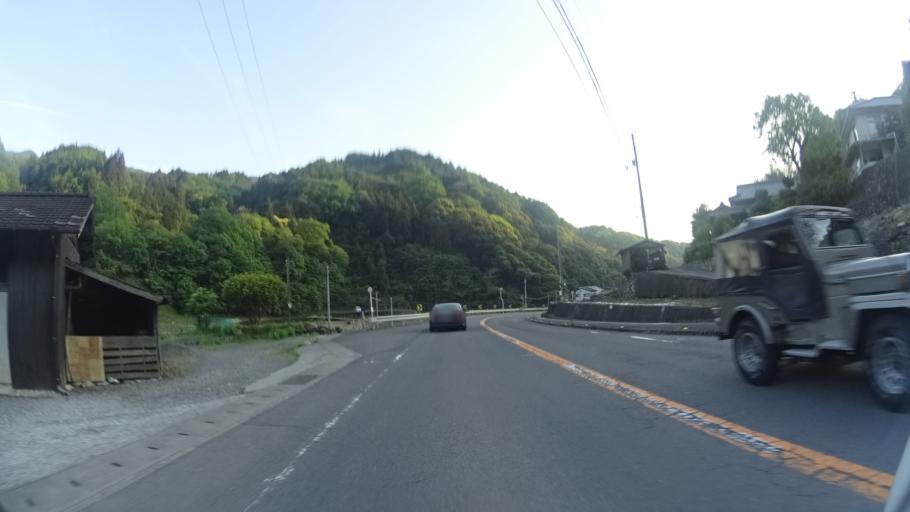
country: JP
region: Ehime
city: Kawanoecho
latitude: 33.9955
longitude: 133.6521
